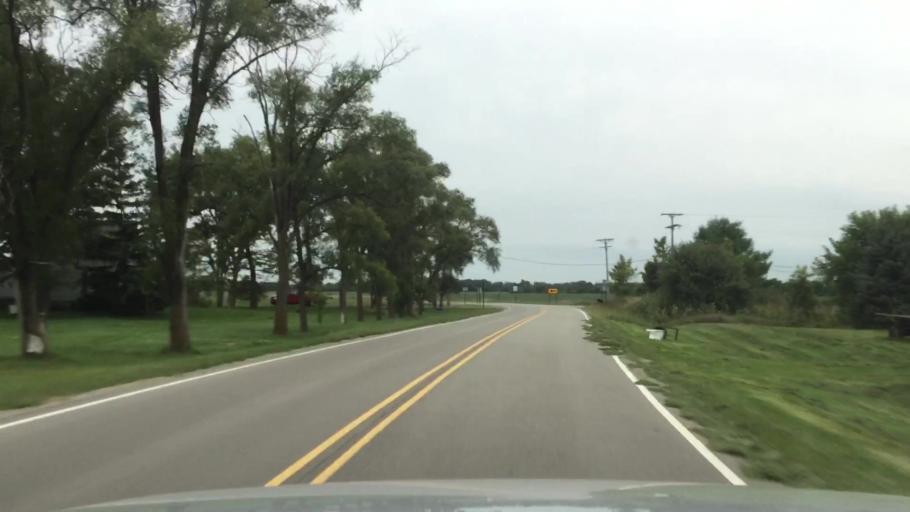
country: US
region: Michigan
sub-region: Washtenaw County
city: Milan
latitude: 42.0841
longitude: -83.7352
